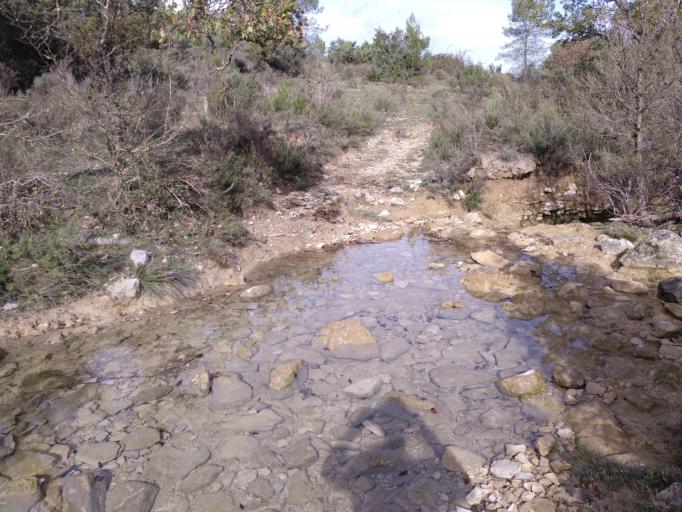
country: FR
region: Languedoc-Roussillon
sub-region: Departement de l'Herault
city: Claret
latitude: 43.8794
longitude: 3.8543
